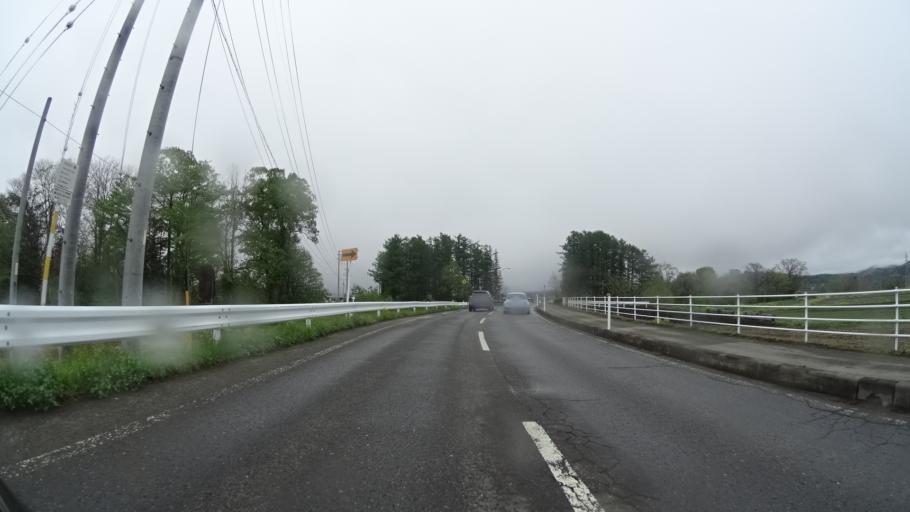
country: JP
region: Nagano
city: Nagano-shi
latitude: 36.7928
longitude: 138.1956
